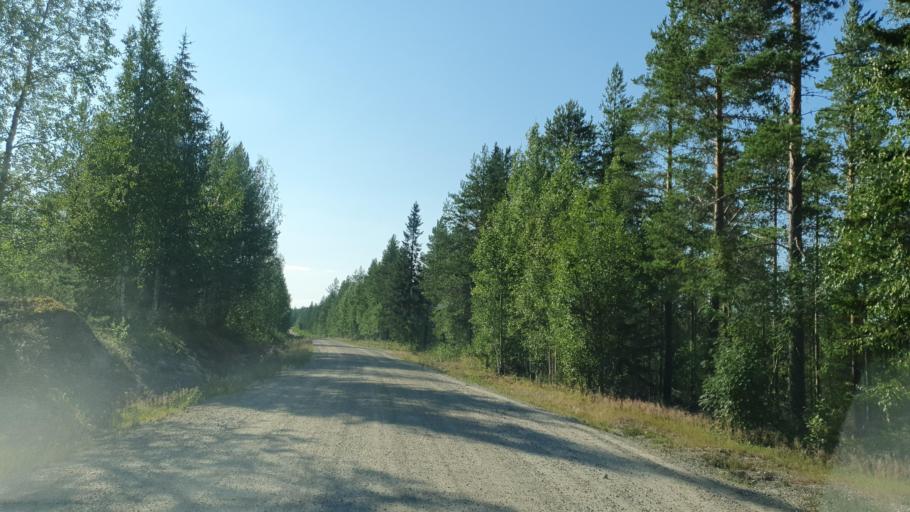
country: FI
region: Kainuu
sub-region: Kehys-Kainuu
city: Kuhmo
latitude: 64.0271
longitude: 29.7136
